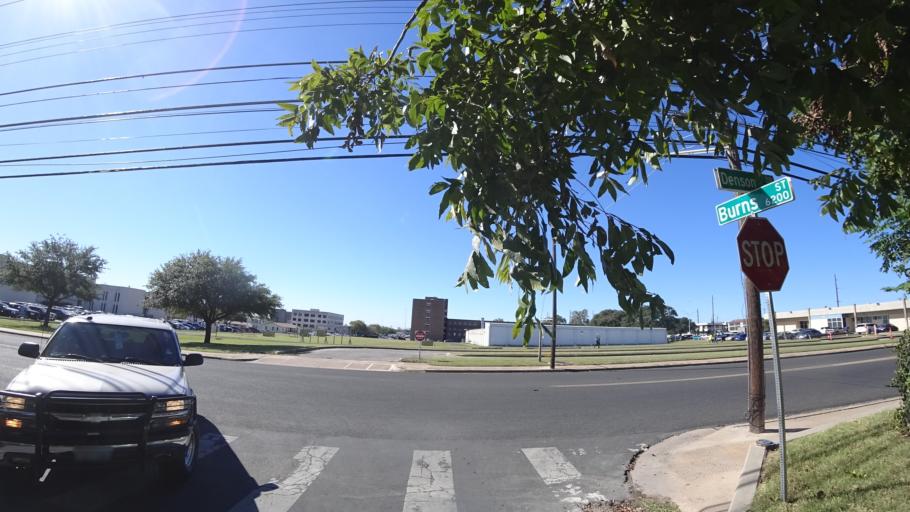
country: US
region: Texas
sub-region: Travis County
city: Austin
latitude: 30.3298
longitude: -97.7221
